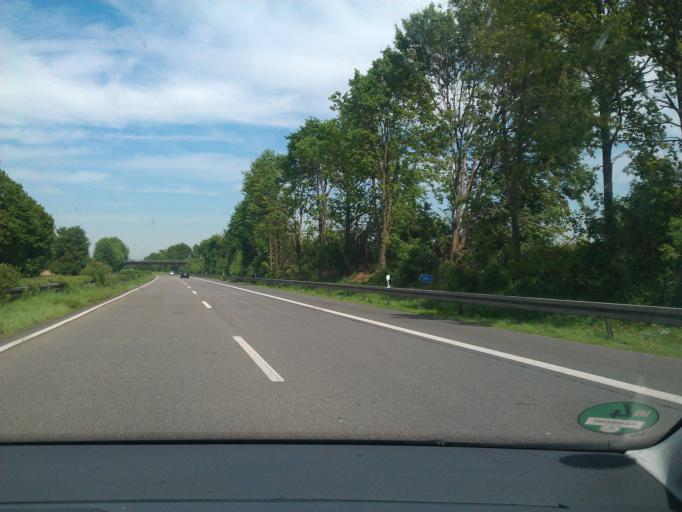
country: DE
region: North Rhine-Westphalia
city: Julich
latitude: 50.9754
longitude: 6.3738
